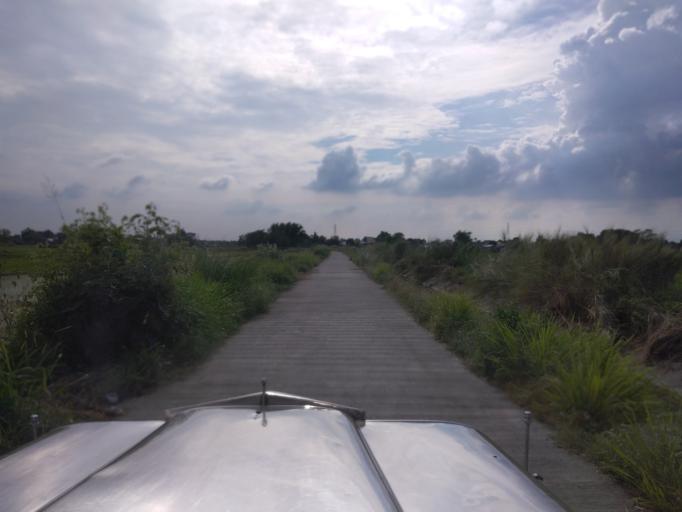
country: PH
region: Central Luzon
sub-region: Province of Pampanga
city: San Patricio
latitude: 15.1100
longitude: 120.7102
